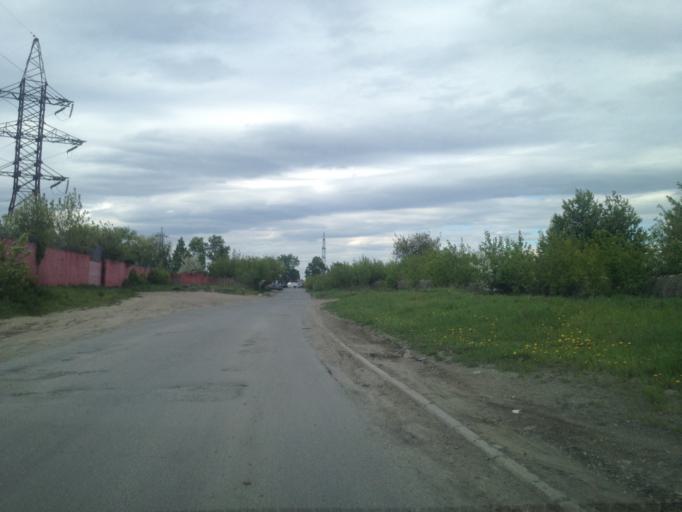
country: RU
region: Sverdlovsk
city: Yekaterinburg
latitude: 56.8774
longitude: 60.5462
